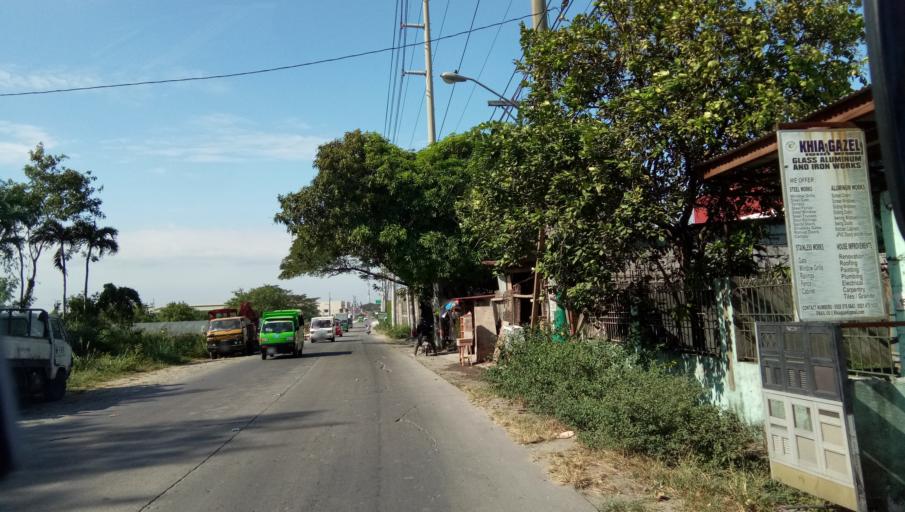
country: PH
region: Calabarzon
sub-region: Province of Cavite
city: Pasong Kawayan Primero
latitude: 14.3496
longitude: 120.9030
